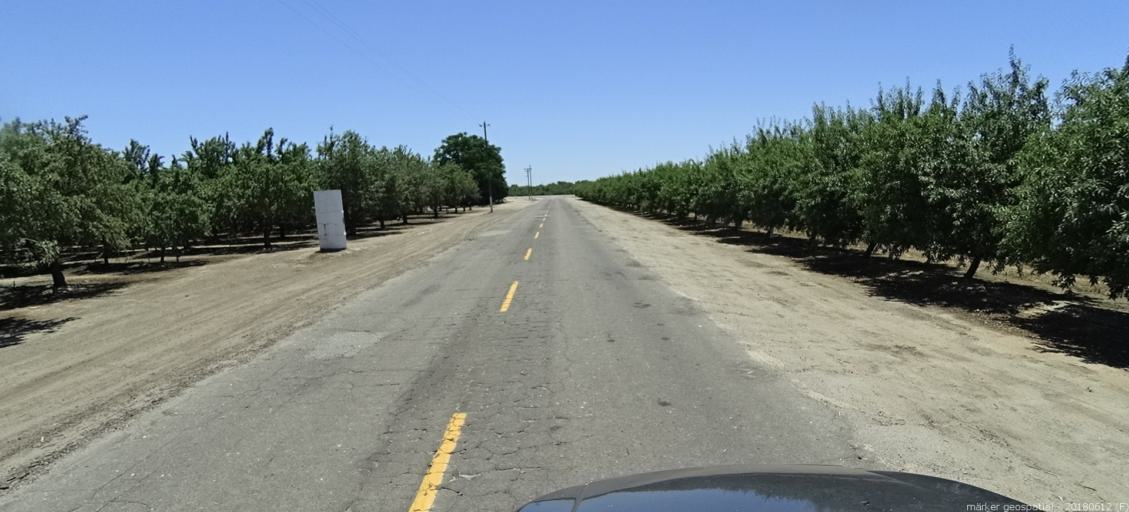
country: US
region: California
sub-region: Madera County
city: Chowchilla
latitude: 37.0856
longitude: -120.2746
